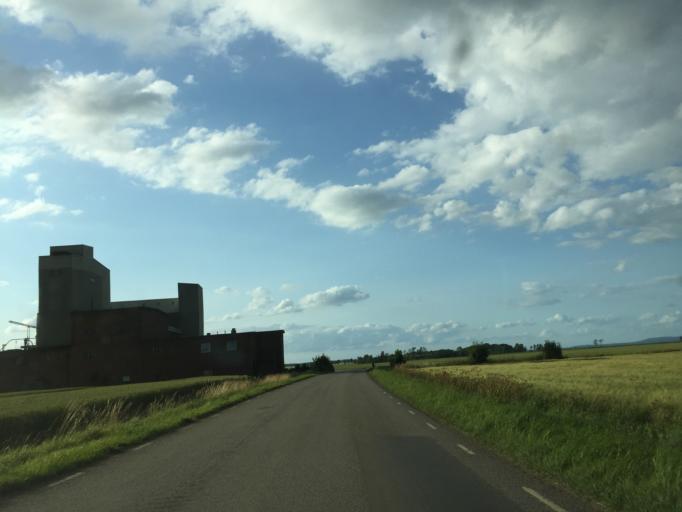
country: SE
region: OEstergoetland
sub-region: Vadstena Kommun
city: Vadstena
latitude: 58.4337
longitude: 14.8545
